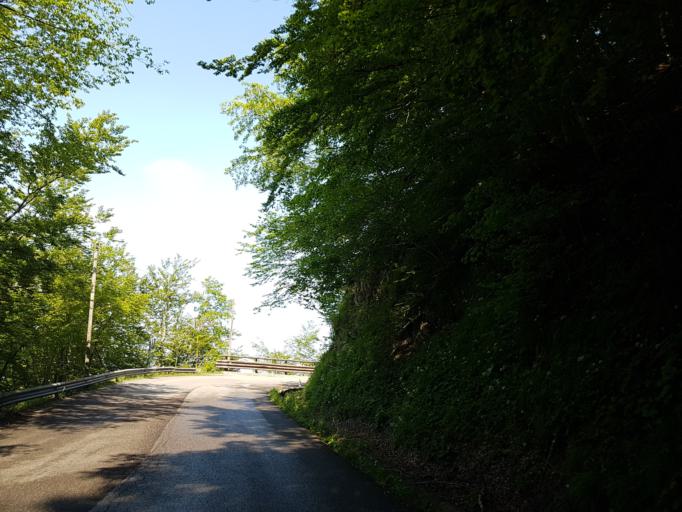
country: IT
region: Emilia-Romagna
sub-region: Forli-Cesena
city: San Piero in Bagno
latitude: 43.8103
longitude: 11.9177
